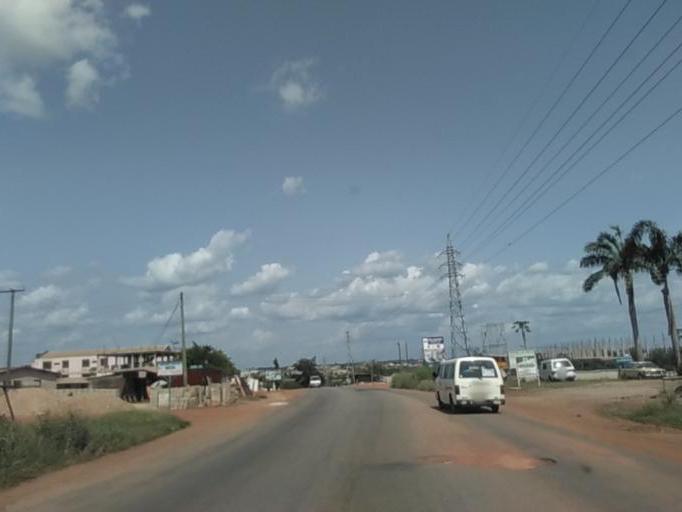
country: GH
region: Ashanti
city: Kumasi
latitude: 6.6380
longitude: -1.5686
